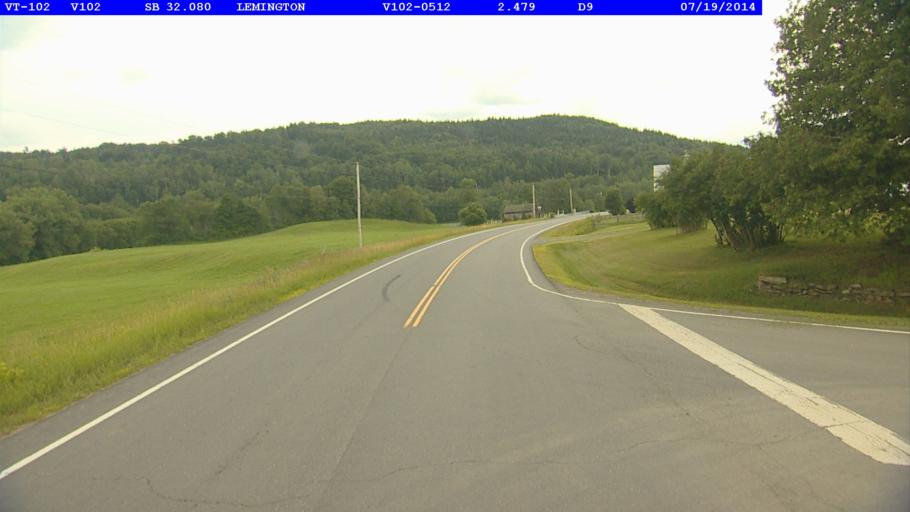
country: US
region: New Hampshire
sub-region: Coos County
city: Colebrook
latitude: 44.8580
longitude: -71.5511
